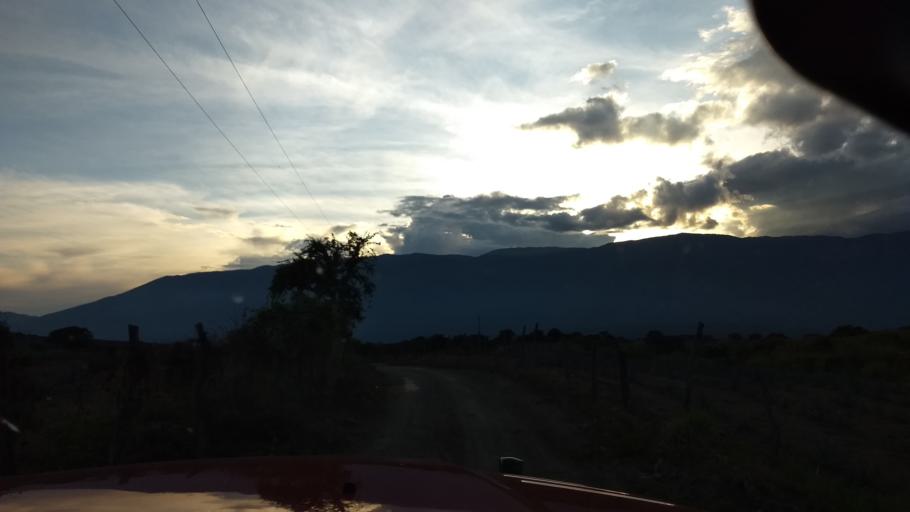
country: MX
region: Colima
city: Suchitlan
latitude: 19.4911
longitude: -103.7870
